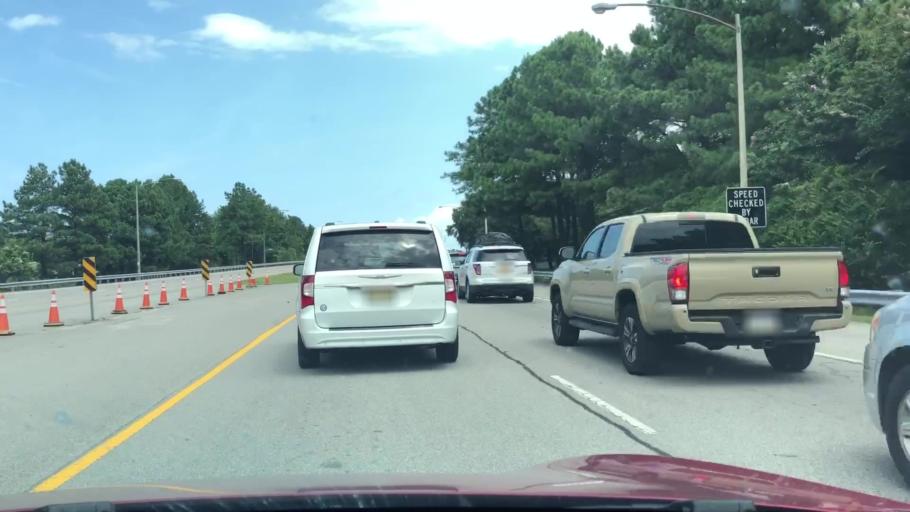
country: US
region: Virginia
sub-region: City of Virginia Beach
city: Virginia Beach
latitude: 36.9145
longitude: -76.1310
